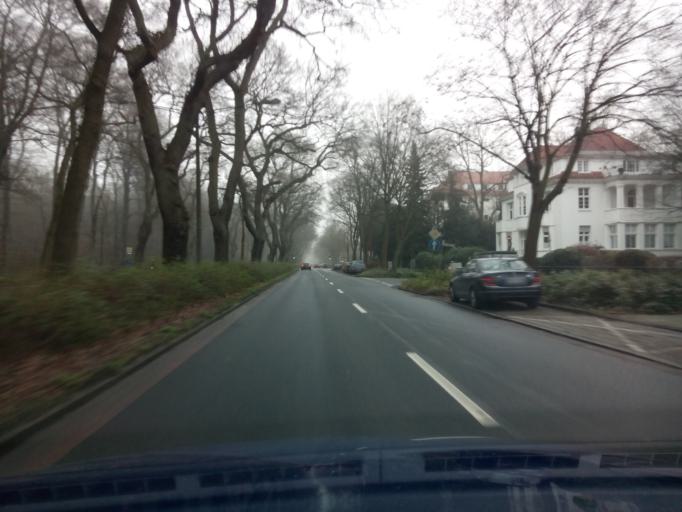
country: DE
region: Bremen
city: Bremen
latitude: 53.0886
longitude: 8.8287
